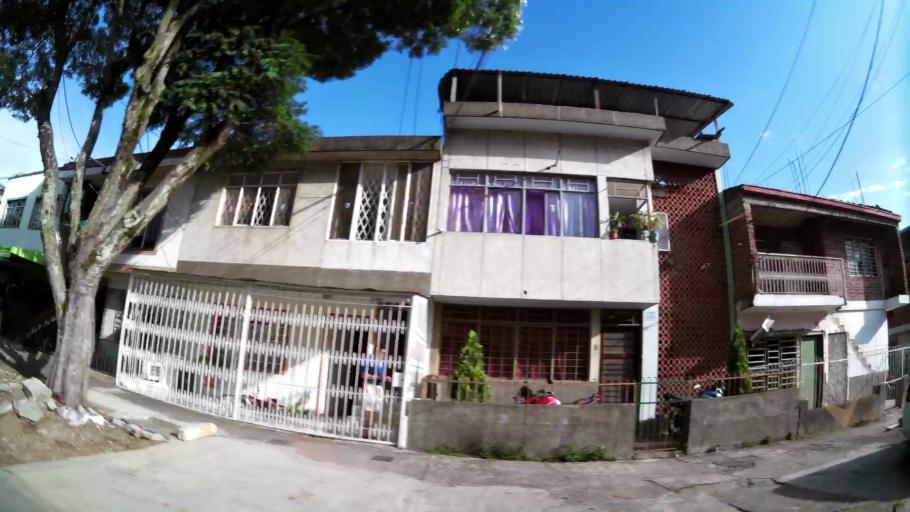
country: CO
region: Valle del Cauca
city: Cali
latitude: 3.4334
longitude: -76.5237
